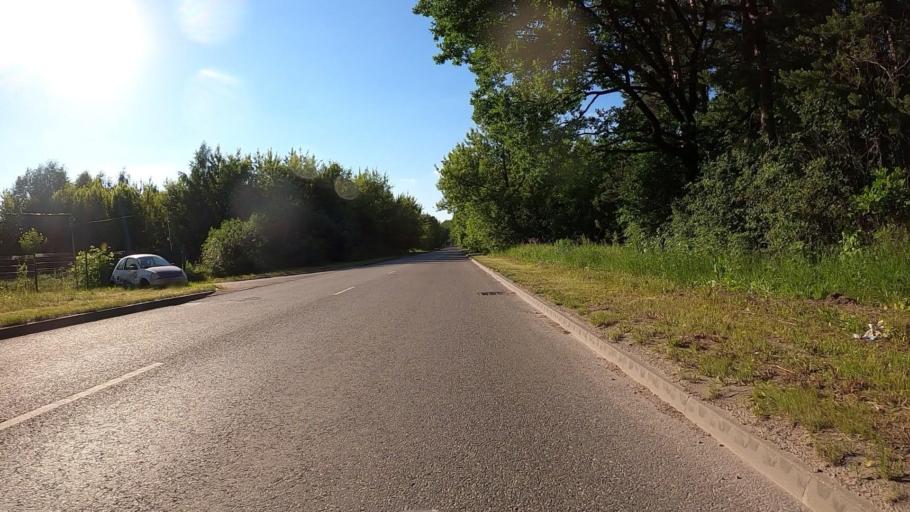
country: LV
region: Kekava
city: Kekava
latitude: 56.8884
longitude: 24.2482
